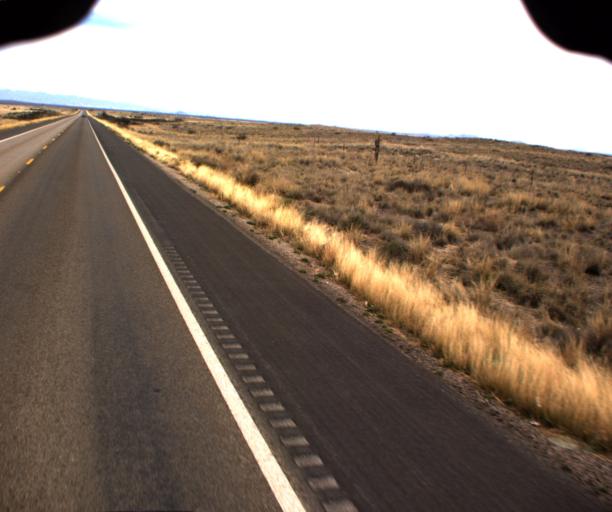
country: US
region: Arizona
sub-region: Cochise County
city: Willcox
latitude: 32.2285
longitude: -109.7990
